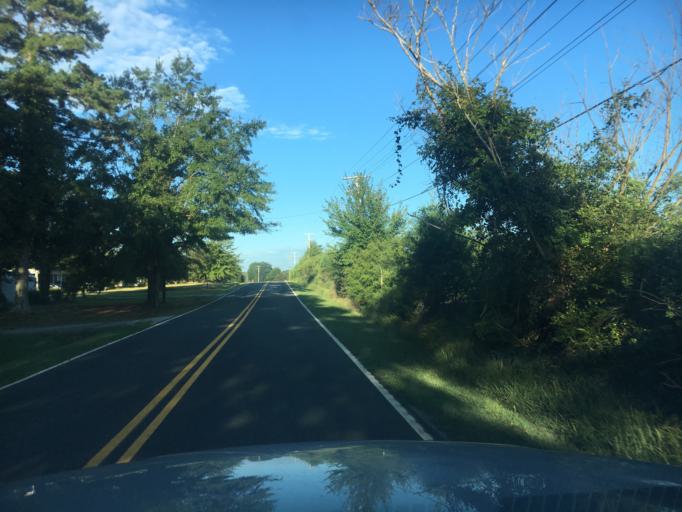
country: US
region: South Carolina
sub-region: Spartanburg County
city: Woodruff
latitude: 34.6348
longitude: -82.0521
